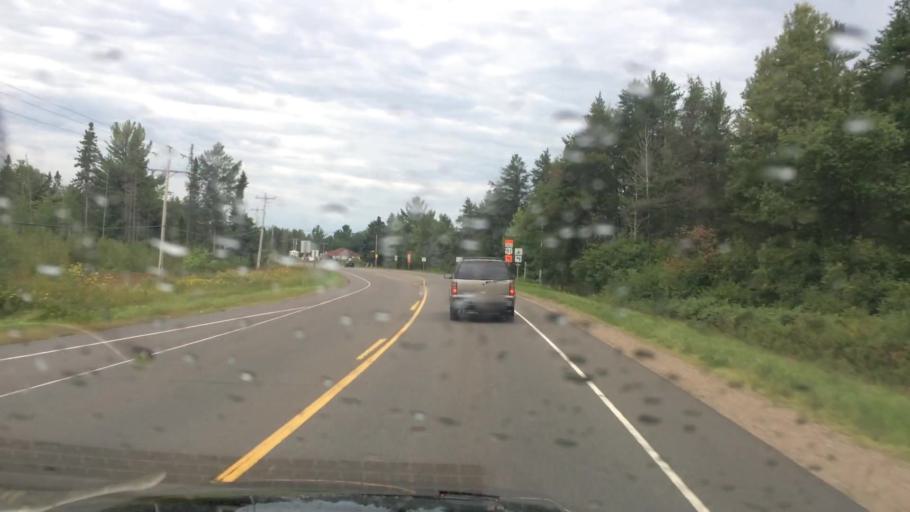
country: US
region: Wisconsin
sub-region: Lincoln County
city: Tomahawk
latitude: 45.4982
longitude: -89.7286
